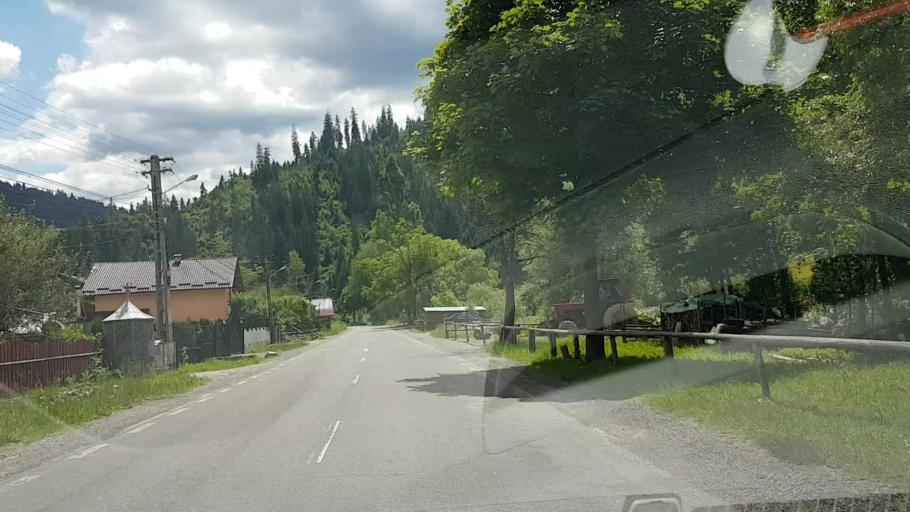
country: RO
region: Suceava
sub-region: Comuna Brosteni
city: Brosteni
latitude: 47.2418
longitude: 25.6910
